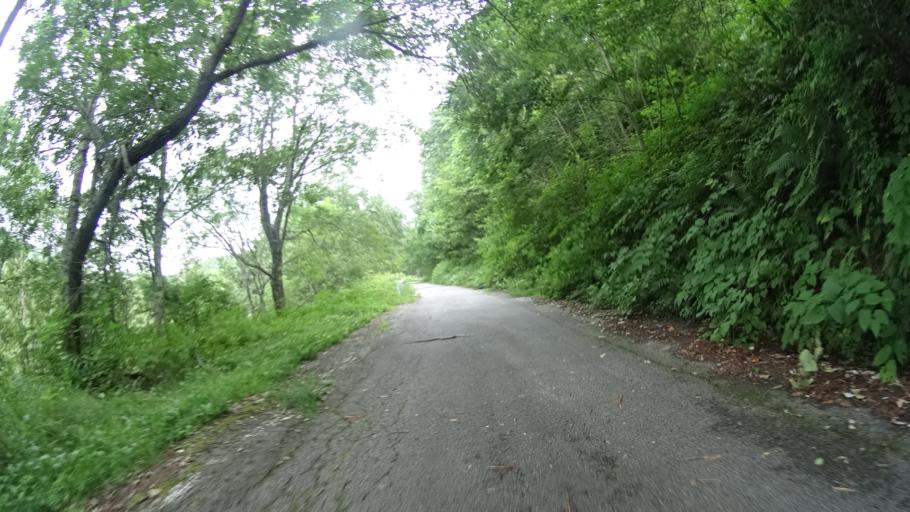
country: JP
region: Yamanashi
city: Enzan
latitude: 35.8081
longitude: 138.6313
